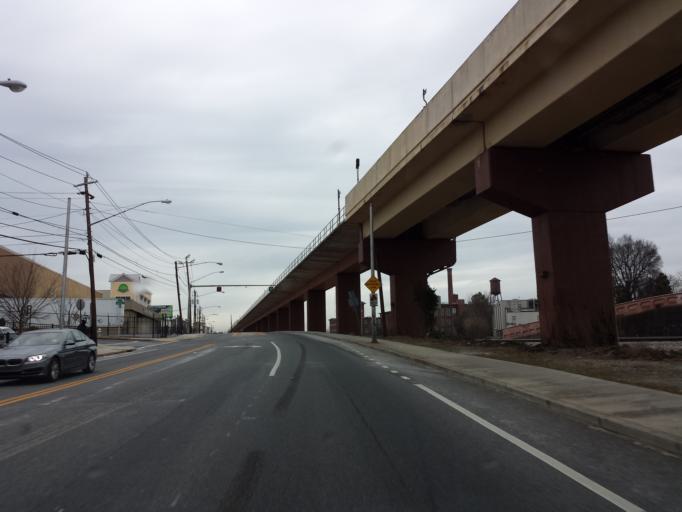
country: US
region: Georgia
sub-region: Fulton County
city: Atlanta
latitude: 33.7506
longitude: -84.3741
